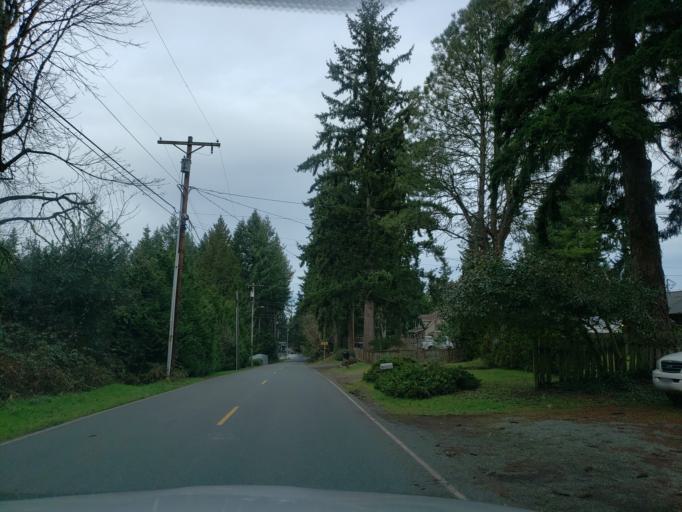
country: US
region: Washington
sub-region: Snohomish County
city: Esperance
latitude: 47.8125
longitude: -122.3441
